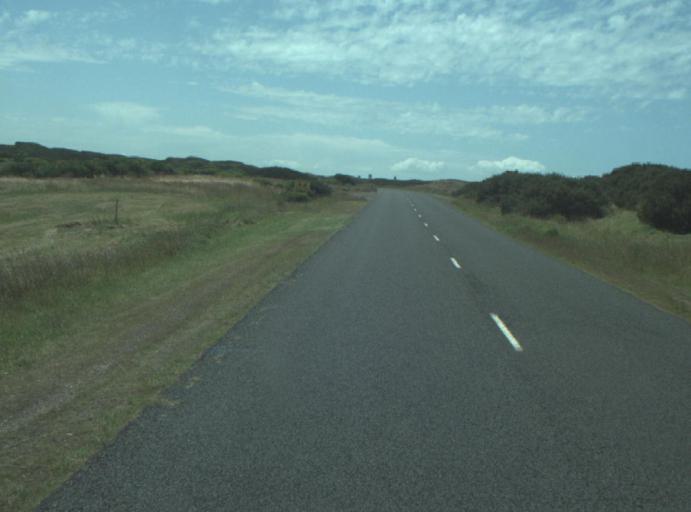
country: AU
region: Victoria
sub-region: Greater Geelong
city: Leopold
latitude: -38.2797
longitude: 144.4259
